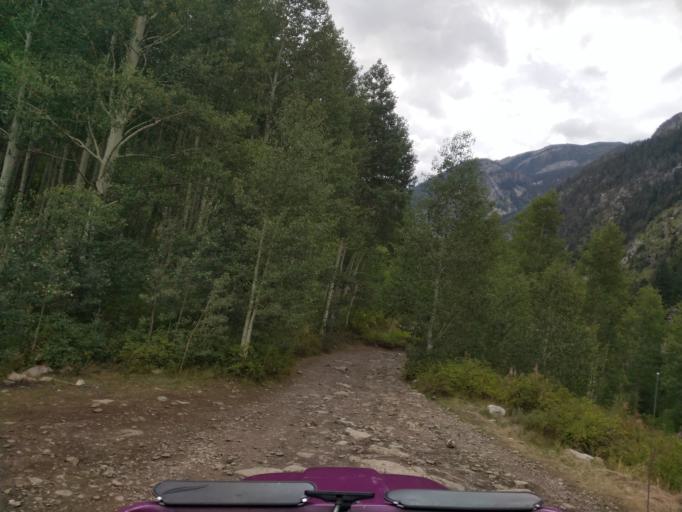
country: US
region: Colorado
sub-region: Gunnison County
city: Crested Butte
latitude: 39.0576
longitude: -107.1354
